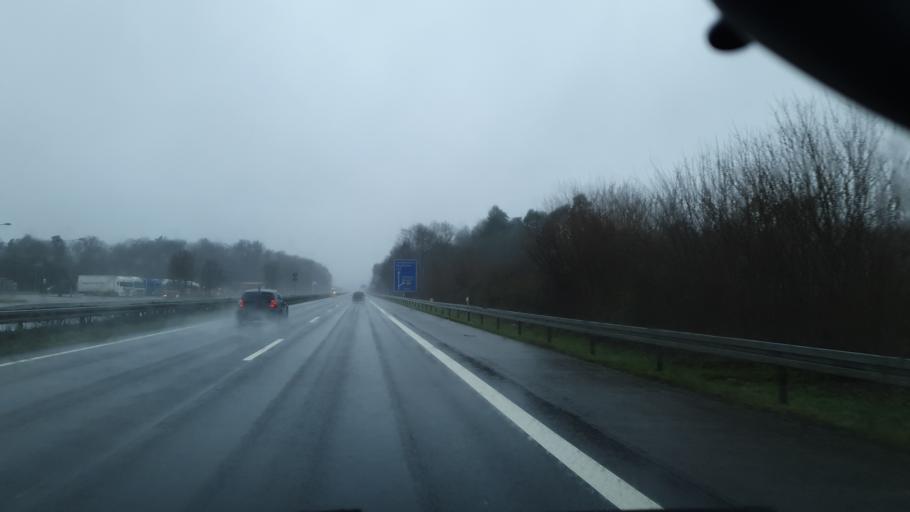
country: DE
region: Saarland
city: Homburg
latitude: 49.3487
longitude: 7.3139
